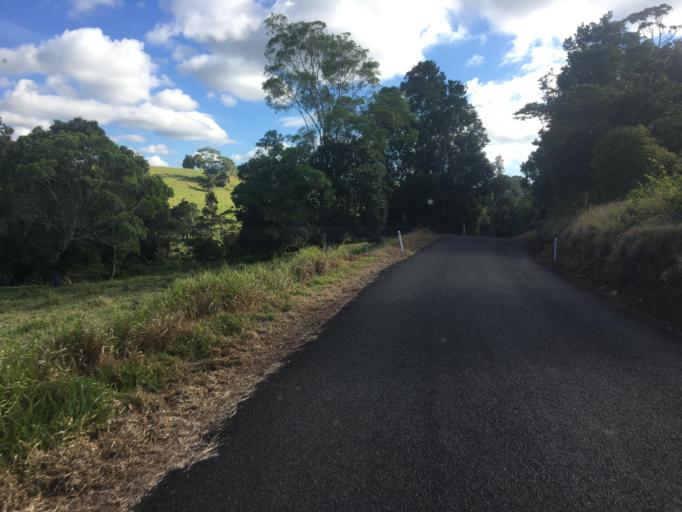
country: AU
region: Queensland
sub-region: Tablelands
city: Ravenshoe
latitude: -17.5852
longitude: 145.6038
